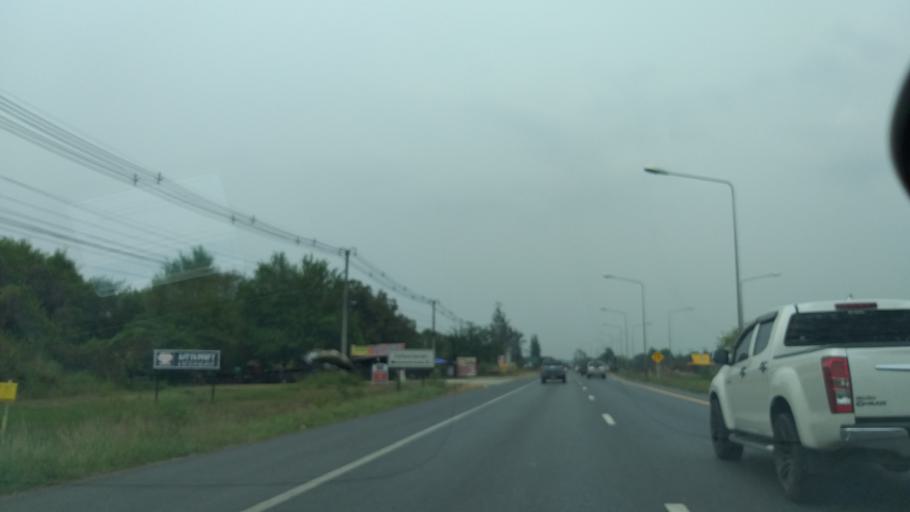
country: TH
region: Chon Buri
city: Ko Chan
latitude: 13.2991
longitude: 101.2614
